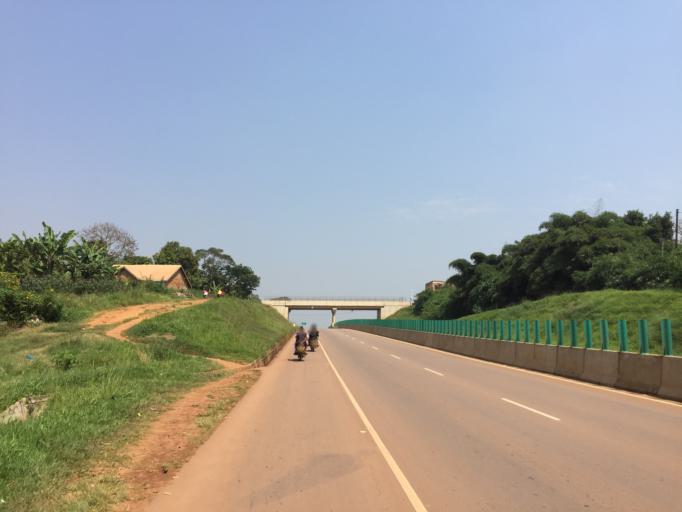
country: UG
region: Central Region
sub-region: Kampala District
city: Kampala
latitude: 0.2381
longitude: 32.6161
